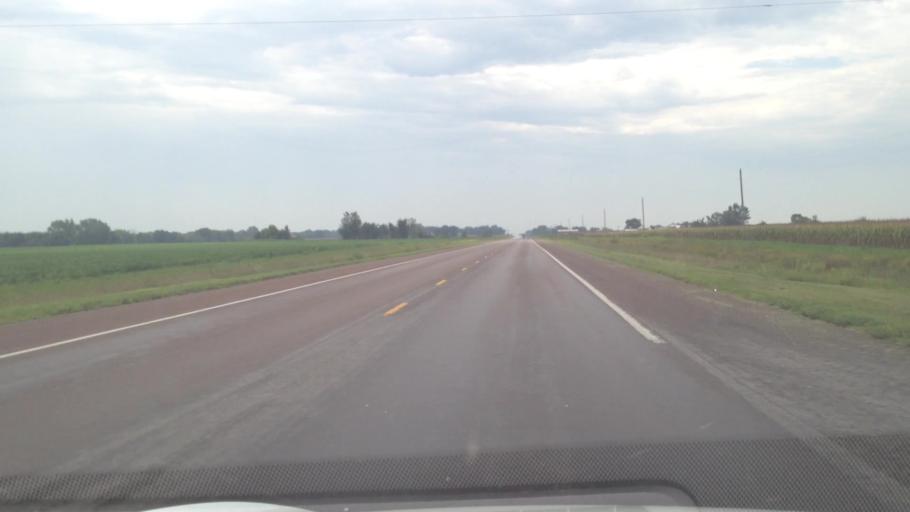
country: US
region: Kansas
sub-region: Crawford County
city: Girard
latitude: 37.4552
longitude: -94.8330
